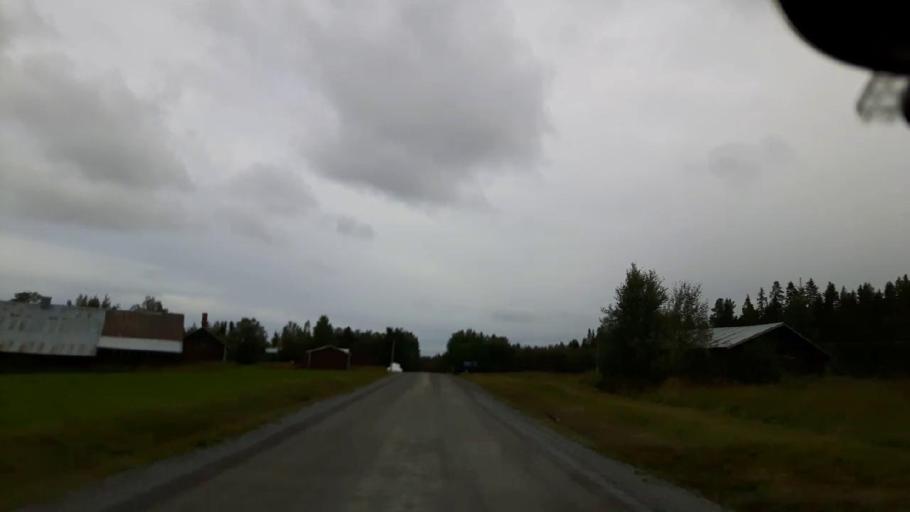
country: SE
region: Jaemtland
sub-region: OEstersunds Kommun
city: Ostersund
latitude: 63.1071
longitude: 14.5460
